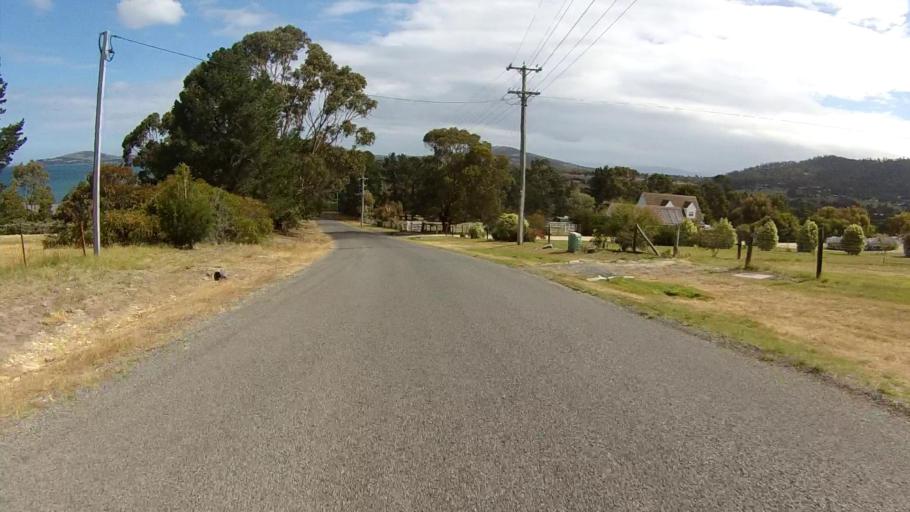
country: AU
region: Tasmania
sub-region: Clarence
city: Acton Park
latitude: -42.8859
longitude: 147.5009
